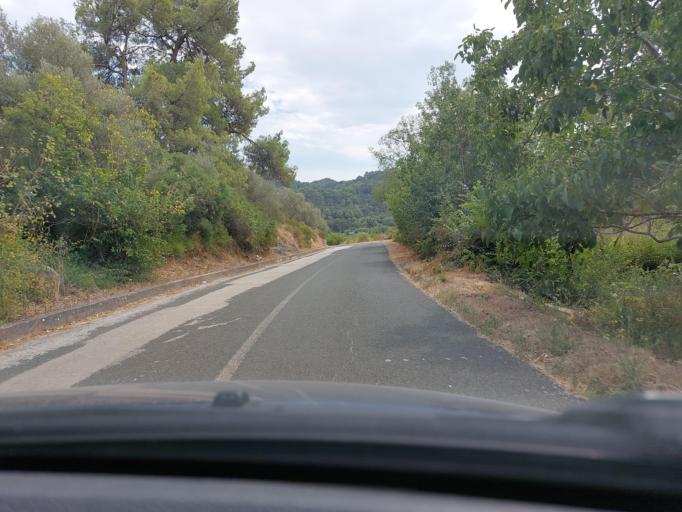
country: HR
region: Dubrovacko-Neretvanska
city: Smokvica
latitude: 42.7641
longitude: 16.8957
